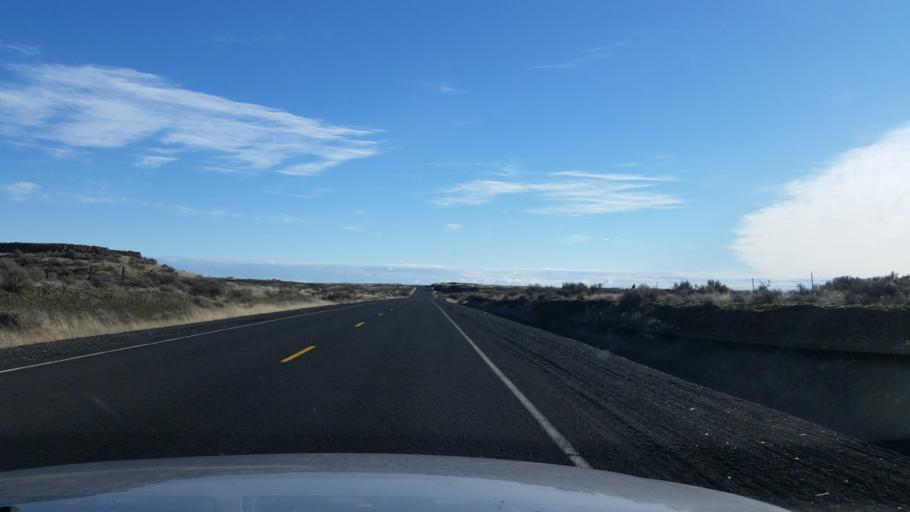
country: US
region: Washington
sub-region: Grant County
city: Warden
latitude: 47.3266
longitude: -118.8710
